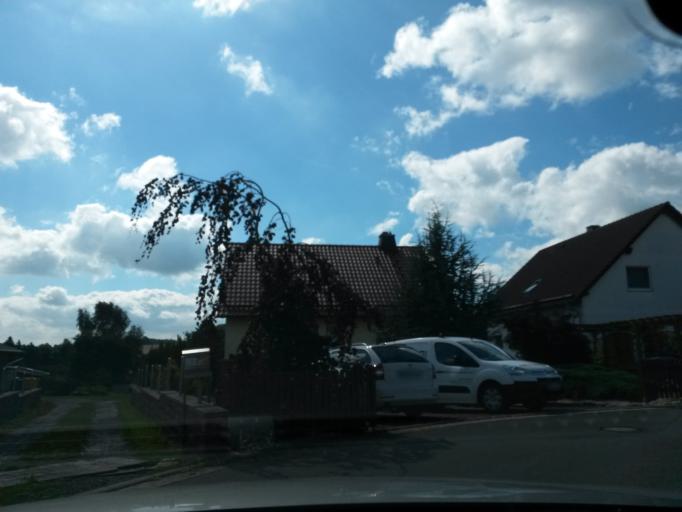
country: DE
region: Thuringia
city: Reichenbach
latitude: 50.8691
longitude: 11.8756
